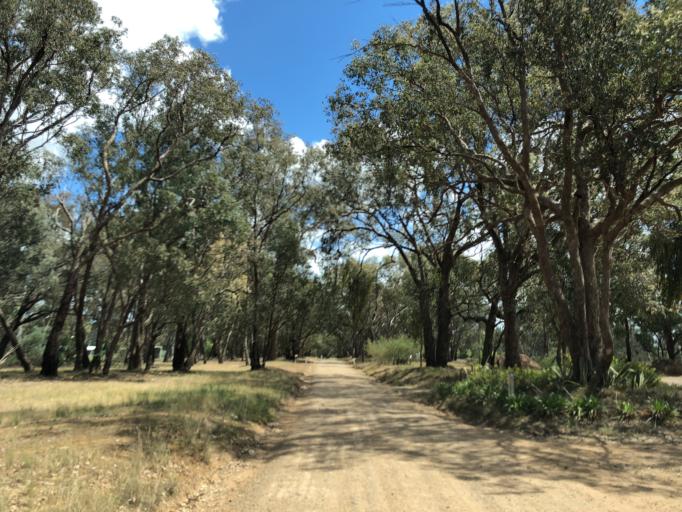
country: AU
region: Victoria
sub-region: Benalla
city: Benalla
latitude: -36.7290
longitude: 146.1168
